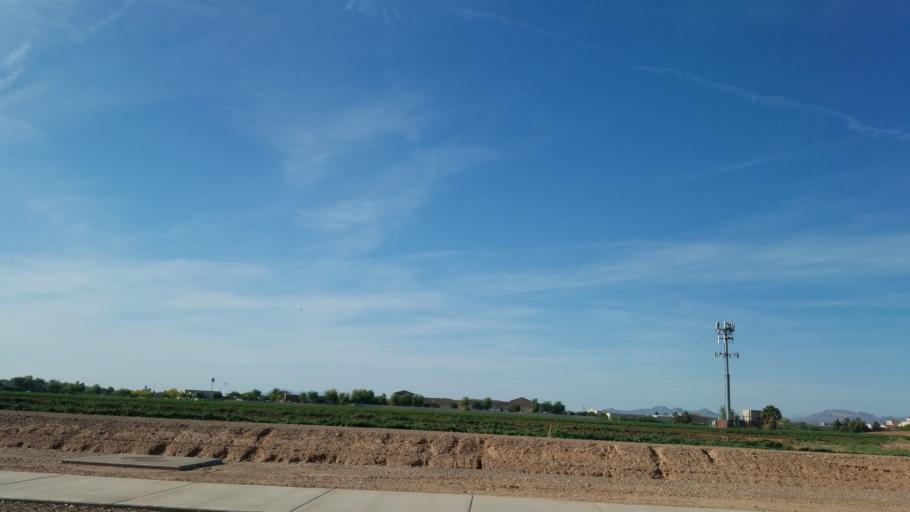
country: US
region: Arizona
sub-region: Maricopa County
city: Queen Creek
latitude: 33.3073
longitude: -111.6916
